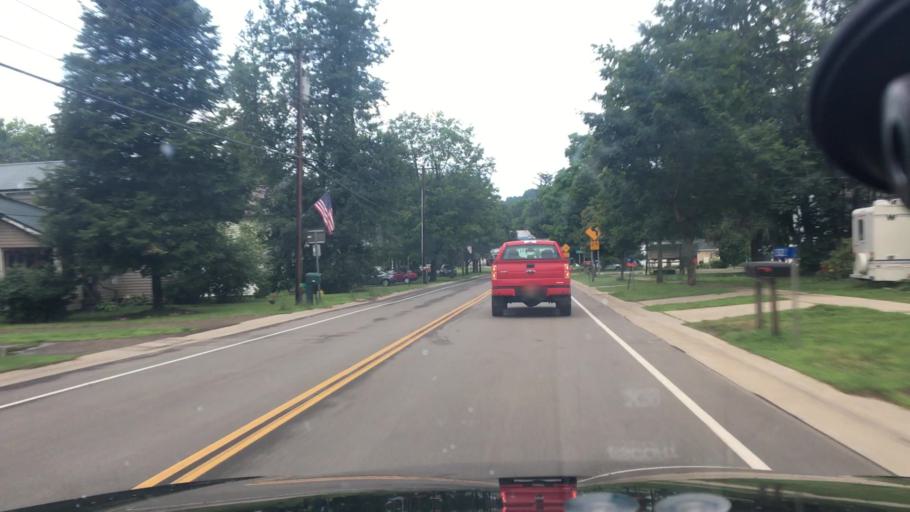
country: US
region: New York
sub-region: Cattaraugus County
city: Randolph
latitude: 42.1726
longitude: -78.9449
